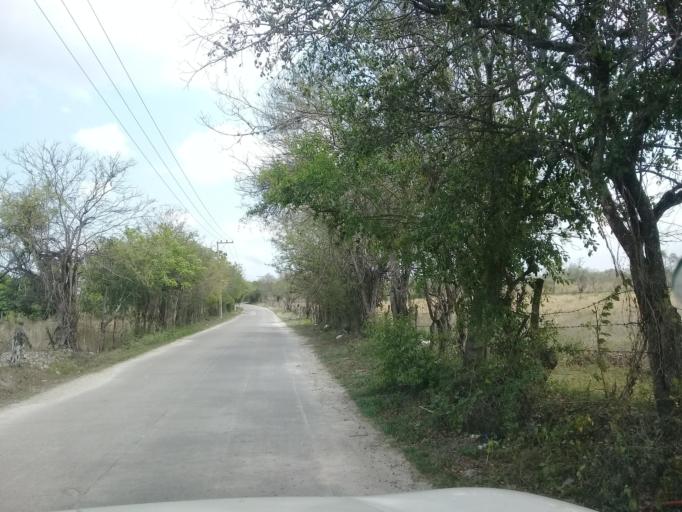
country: MX
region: Veracruz
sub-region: Emiliano Zapata
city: Plan del Rio
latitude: 19.3580
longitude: -96.6543
